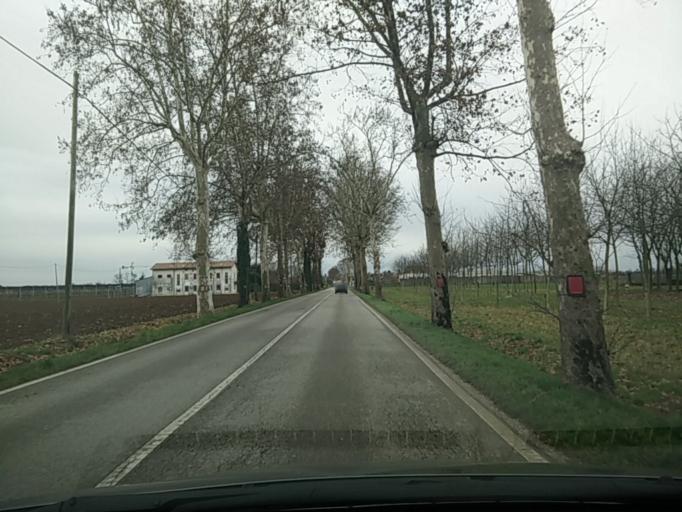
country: IT
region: Veneto
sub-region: Provincia di Treviso
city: Villa d'Asolo
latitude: 45.7661
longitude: 11.9104
